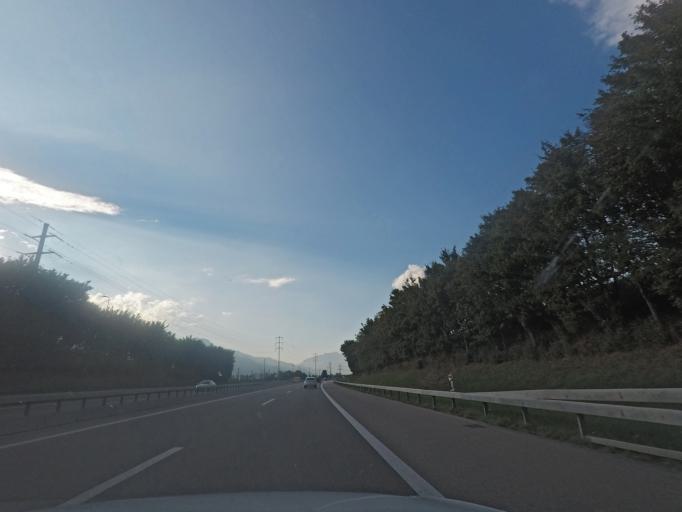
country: CH
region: Saint Gallen
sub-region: Wahlkreis Sarganserland
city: Bad Ragaz
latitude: 47.0169
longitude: 9.4935
